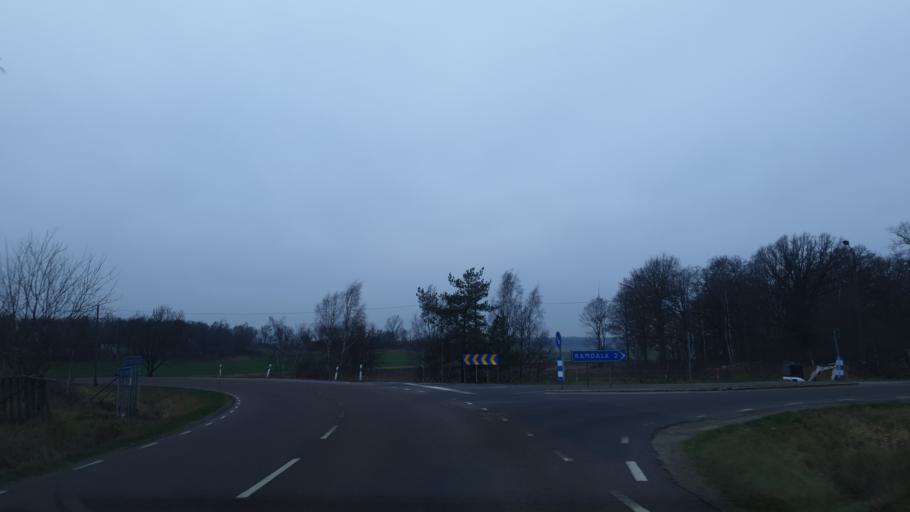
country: SE
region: Blekinge
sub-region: Karlskrona Kommun
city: Jaemjoe
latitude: 56.1663
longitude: 15.7597
